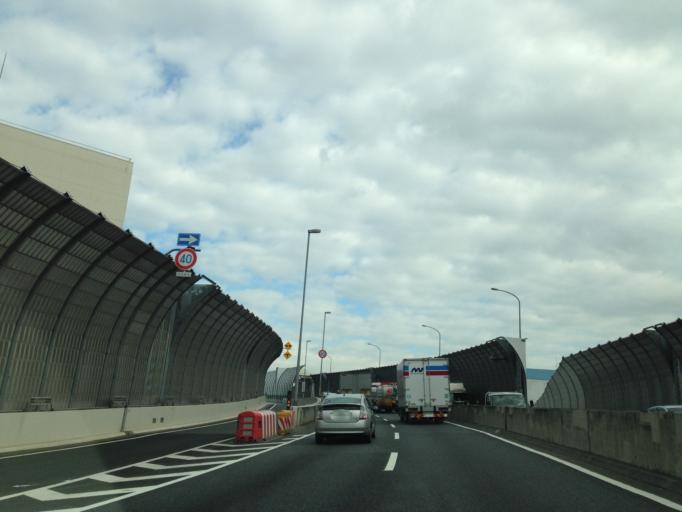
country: JP
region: Saitama
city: Kawaguchi
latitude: 35.7528
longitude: 139.7411
